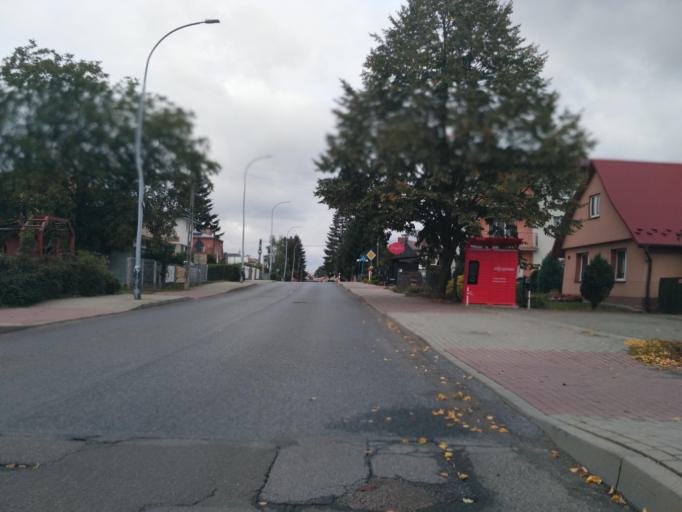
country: PL
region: Subcarpathian Voivodeship
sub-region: Krosno
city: Krosno
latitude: 49.6880
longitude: 21.7821
